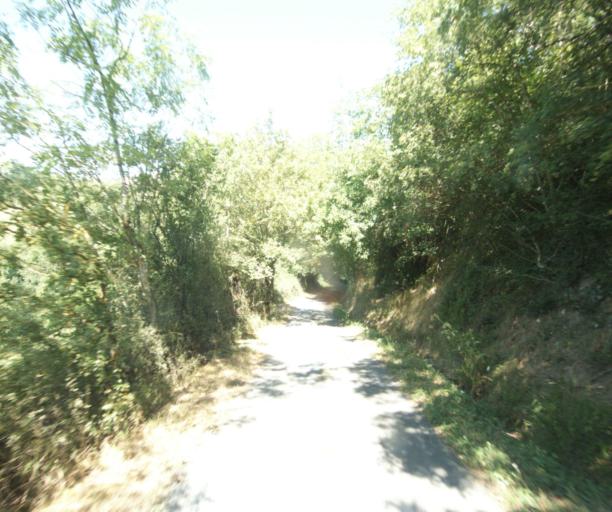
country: FR
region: Rhone-Alpes
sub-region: Departement du Rhone
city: Bessenay
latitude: 45.7942
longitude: 4.5278
